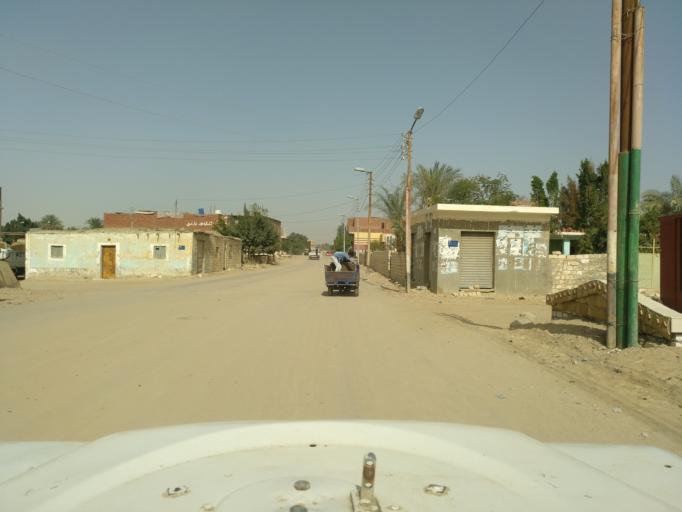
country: EG
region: Al Buhayrah
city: Beheira
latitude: 30.3836
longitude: 30.3417
